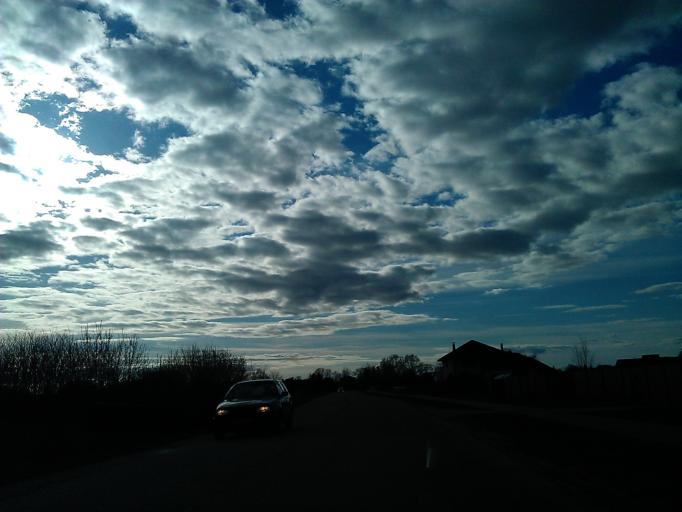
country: LV
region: Adazi
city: Adazi
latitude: 57.0697
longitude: 24.3431
